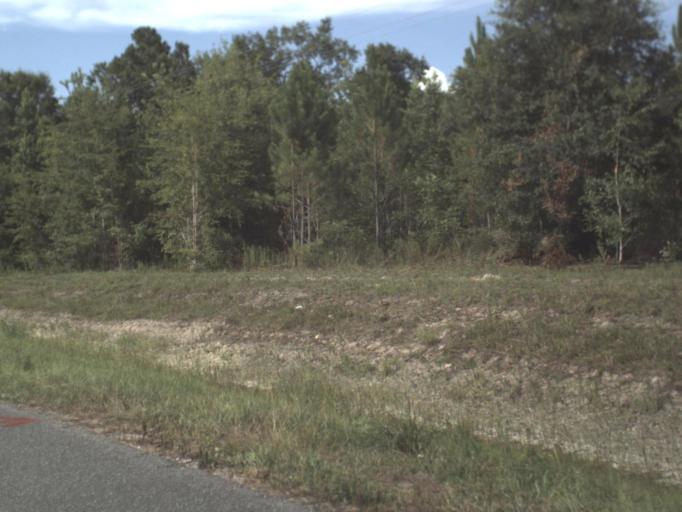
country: US
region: Florida
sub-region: Taylor County
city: Perry
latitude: 30.2429
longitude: -83.6204
